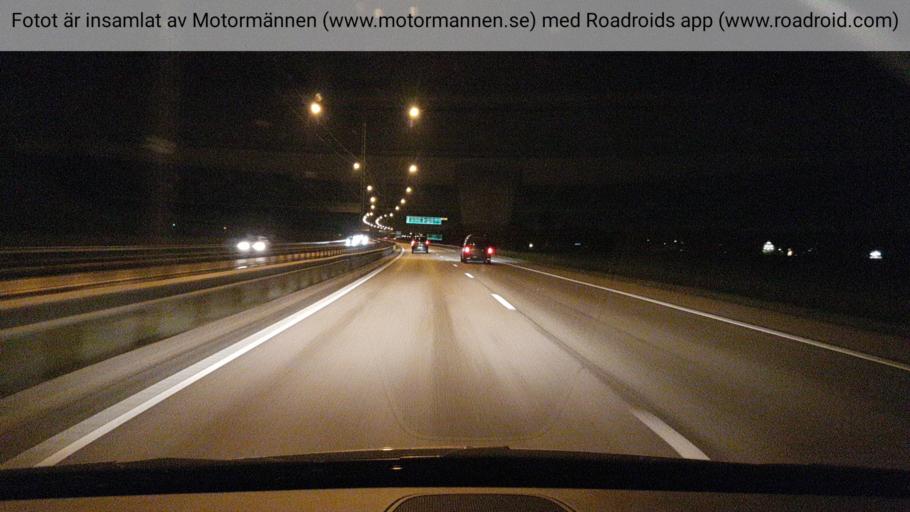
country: SE
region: Stockholm
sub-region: Sigtuna Kommun
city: Rosersberg
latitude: 59.5917
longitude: 17.8966
